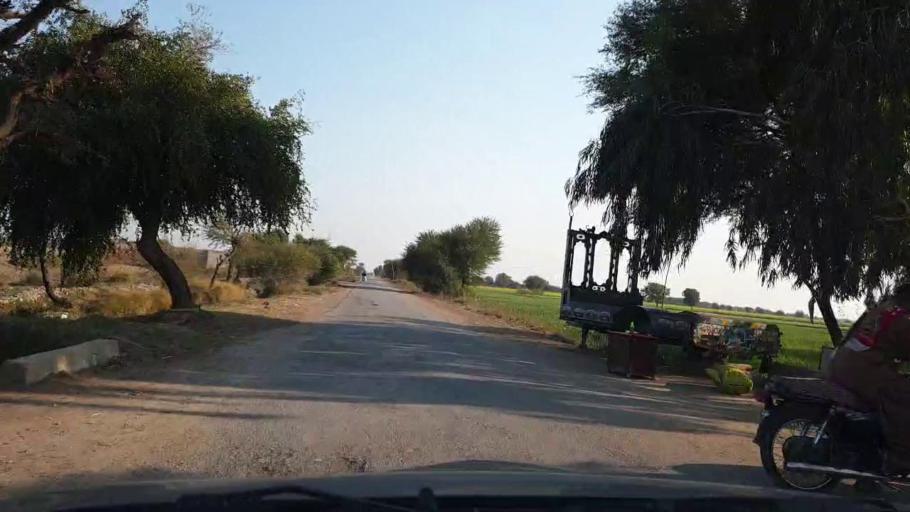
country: PK
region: Sindh
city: Jhol
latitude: 25.9535
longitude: 68.8997
